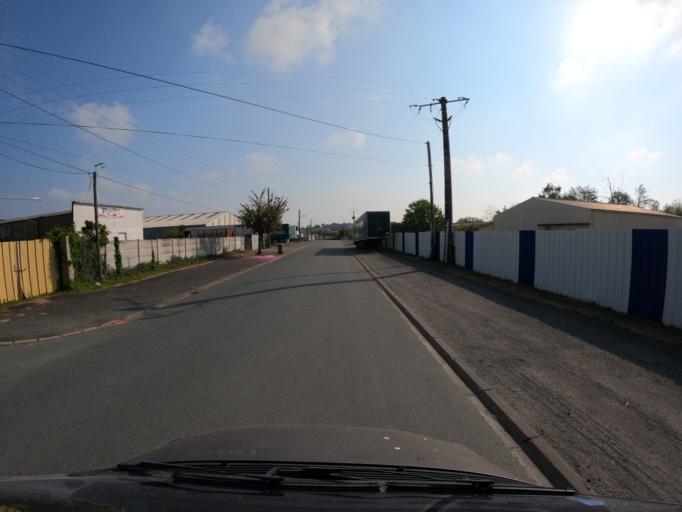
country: FR
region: Pays de la Loire
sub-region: Departement de Maine-et-Loire
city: La Romagne
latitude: 47.0572
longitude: -1.0134
